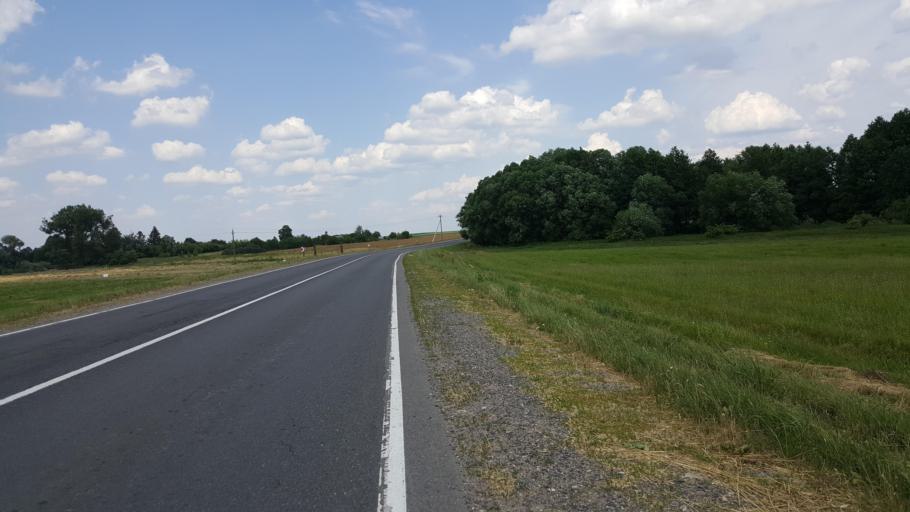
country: BY
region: Brest
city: Kamyanyets
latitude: 52.4028
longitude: 23.7841
